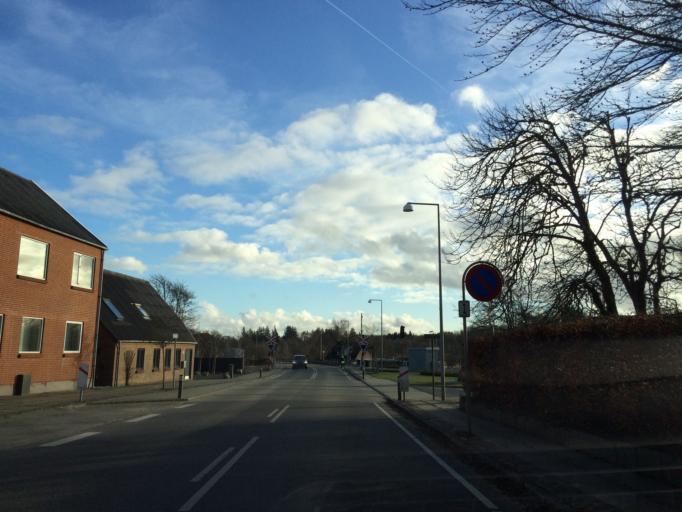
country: DK
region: Central Jutland
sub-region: Lemvig Kommune
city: Lemvig
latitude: 56.4123
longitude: 8.3089
